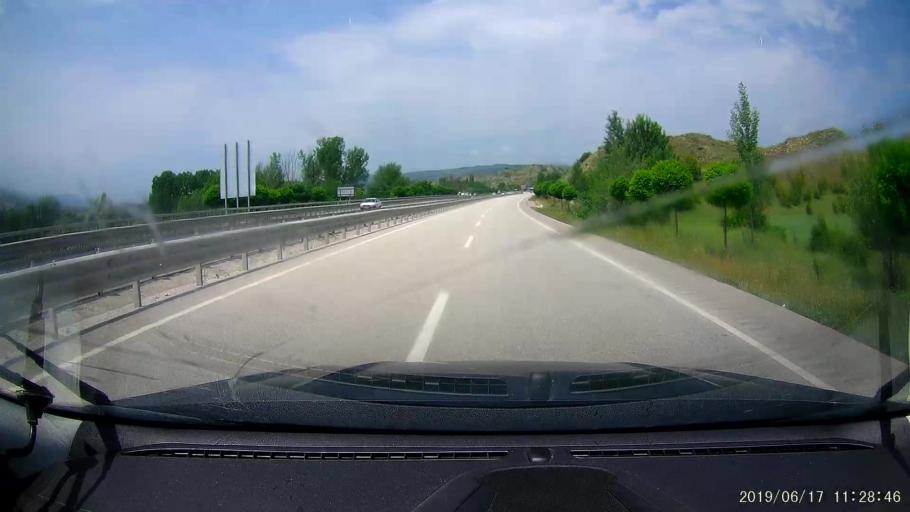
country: TR
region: Cankiri
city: Ilgaz
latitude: 40.9074
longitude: 33.6131
